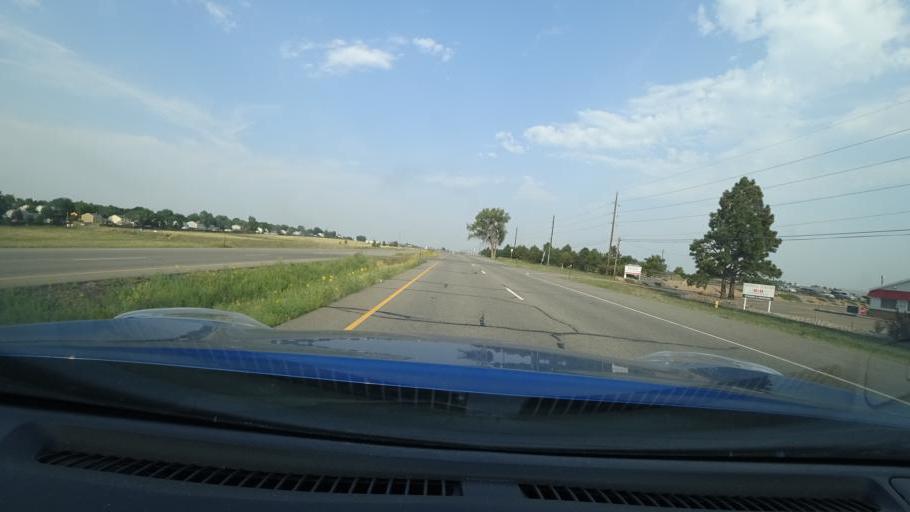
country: US
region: Colorado
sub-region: Adams County
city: Aurora
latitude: 39.7402
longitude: -104.7542
